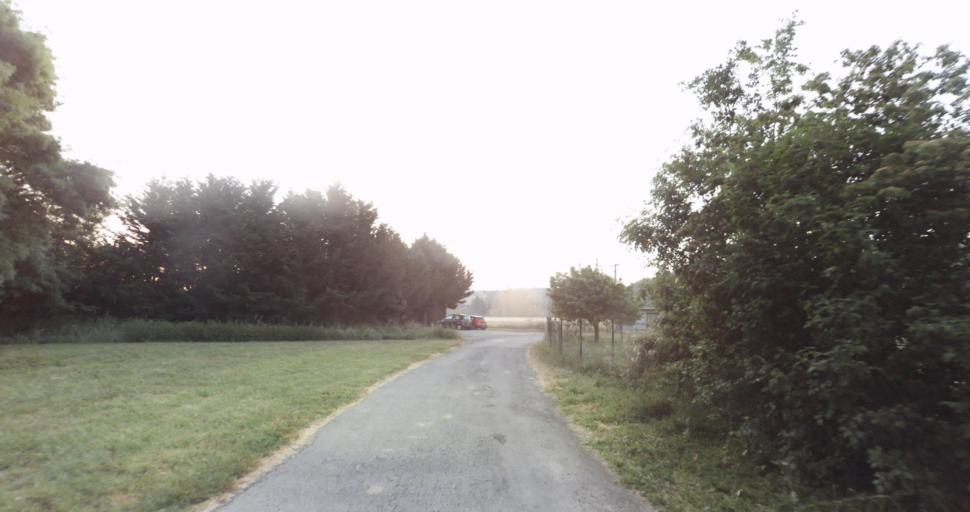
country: FR
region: Midi-Pyrenees
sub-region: Departement de la Haute-Garonne
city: Levignac
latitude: 43.6691
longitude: 1.1934
